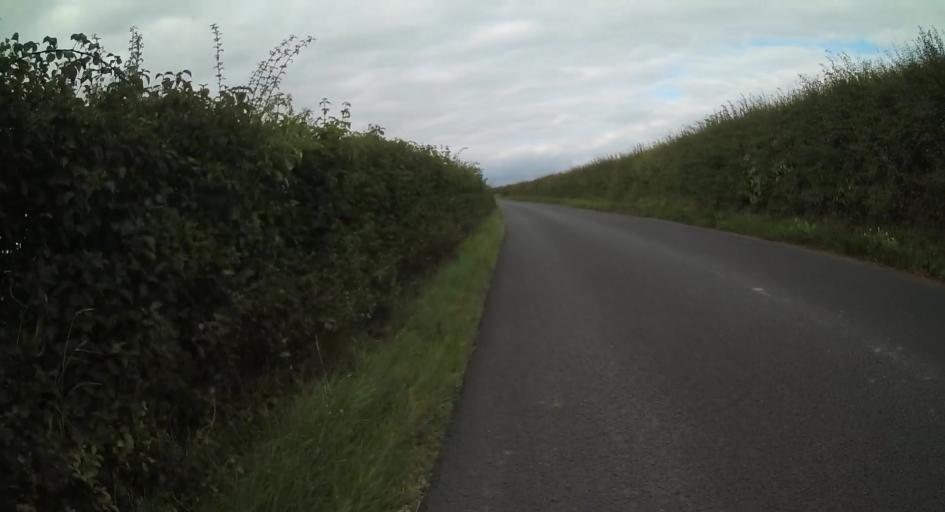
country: GB
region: England
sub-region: Isle of Wight
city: Yarmouth
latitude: 50.6944
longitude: -1.4836
